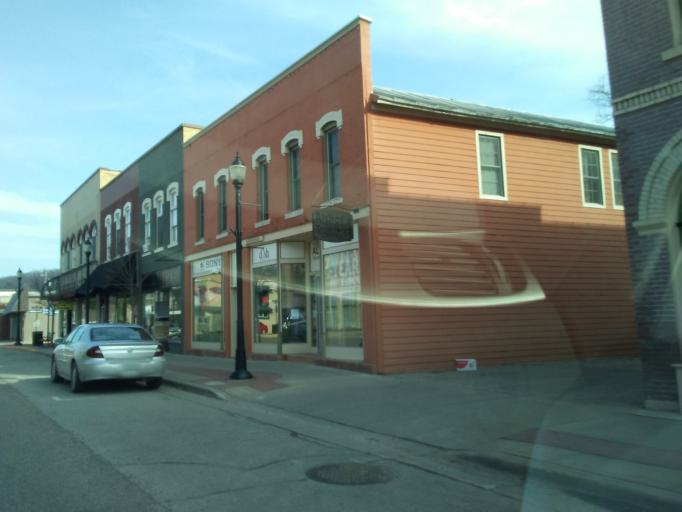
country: US
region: Wisconsin
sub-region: Crawford County
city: Prairie du Chien
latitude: 43.0517
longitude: -91.1459
